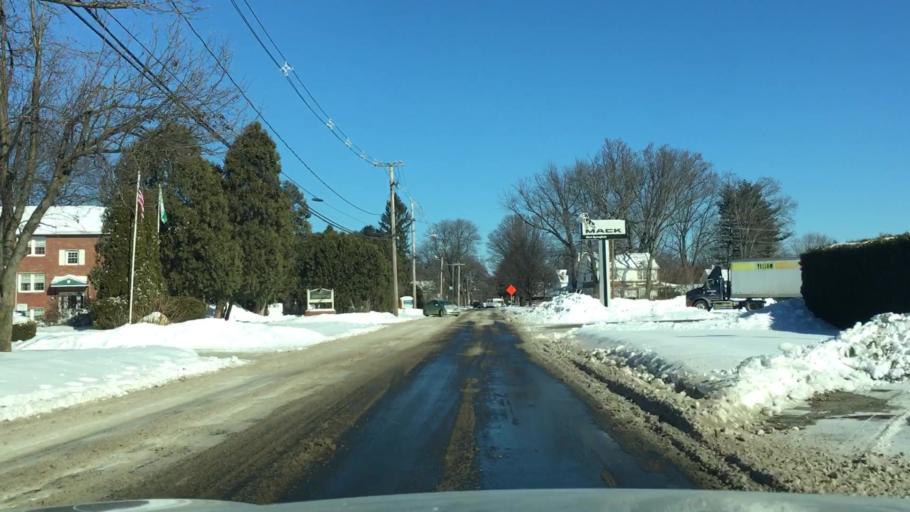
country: US
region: Massachusetts
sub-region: Hampden County
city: Chicopee
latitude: 42.1396
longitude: -72.6236
